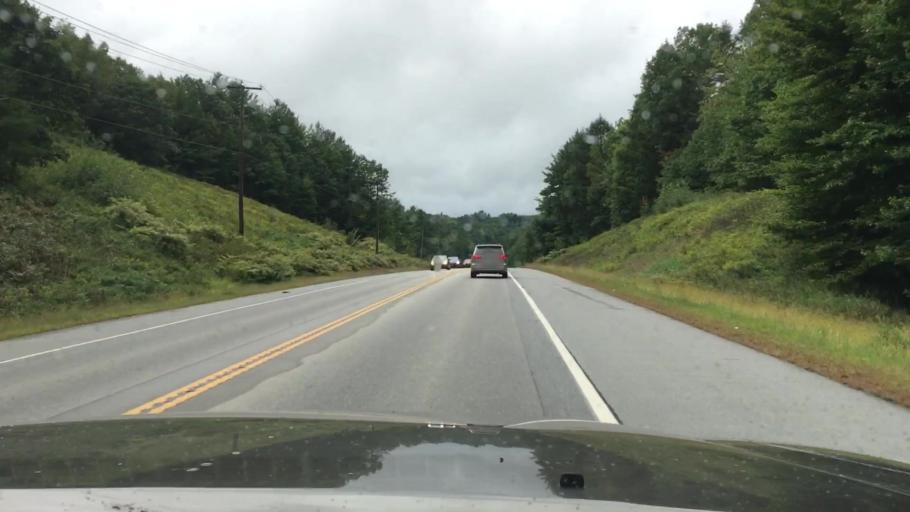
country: US
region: New Hampshire
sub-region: Cheshire County
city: Chesterfield
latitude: 42.8994
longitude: -72.4342
